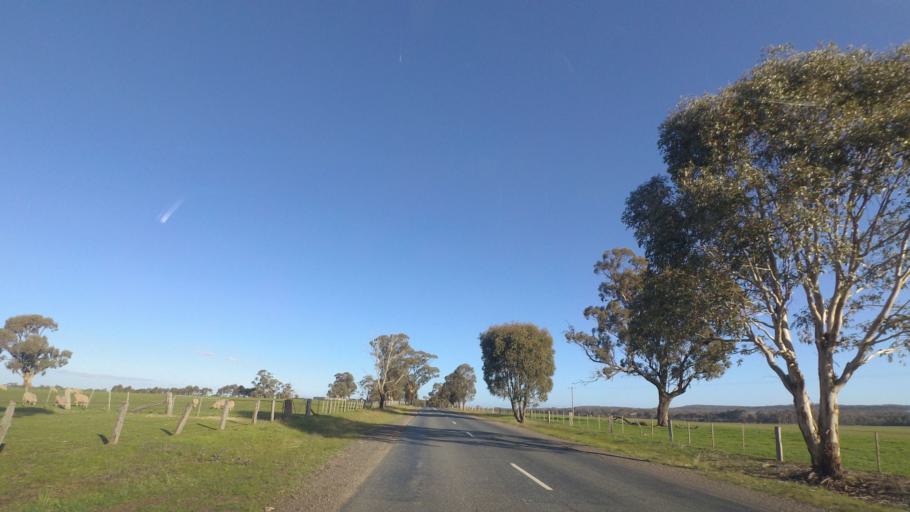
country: AU
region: Victoria
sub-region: Greater Bendigo
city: Epsom
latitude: -36.7126
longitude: 144.5138
